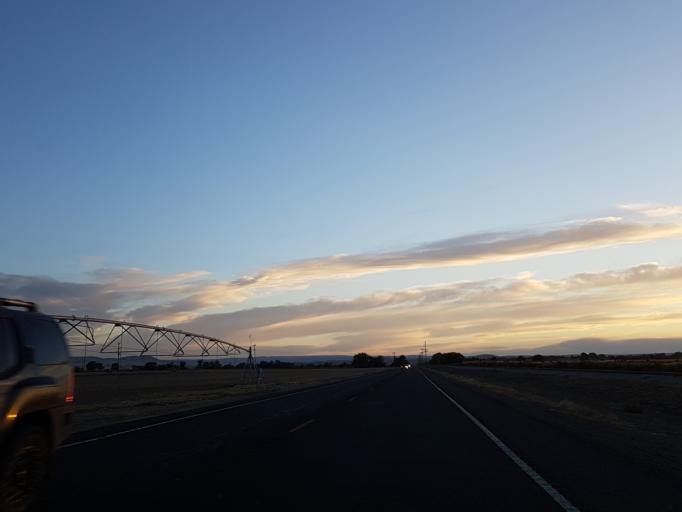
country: US
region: Oregon
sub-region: Malheur County
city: Vale
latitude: 43.9778
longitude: -117.2585
